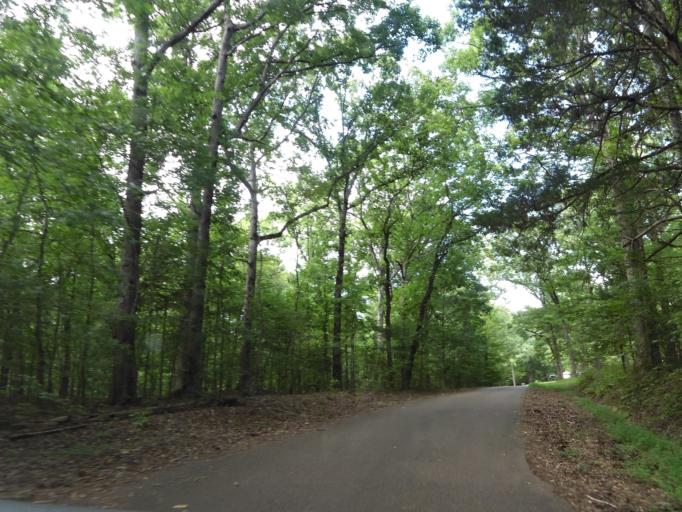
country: US
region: Tennessee
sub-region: Hardin County
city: Crump
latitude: 35.1462
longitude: -88.3204
